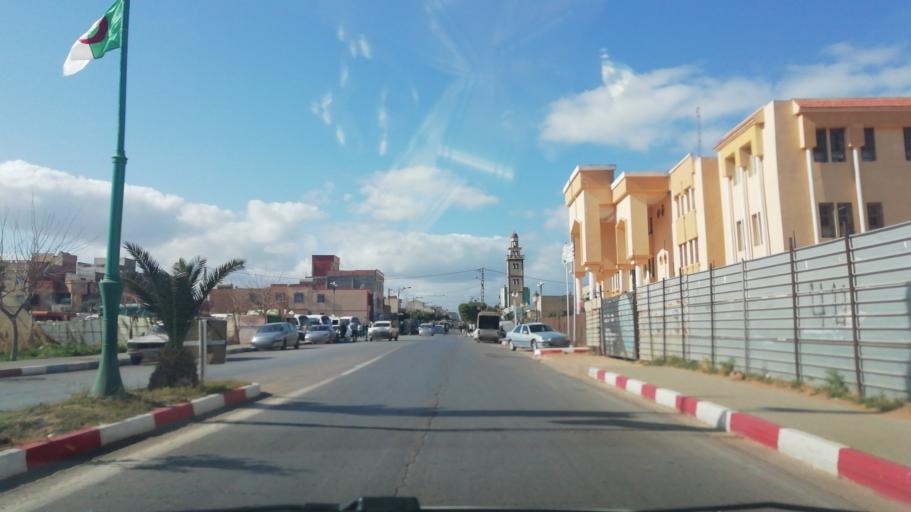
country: DZ
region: Relizane
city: Mazouna
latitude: 36.3203
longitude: 0.6716
